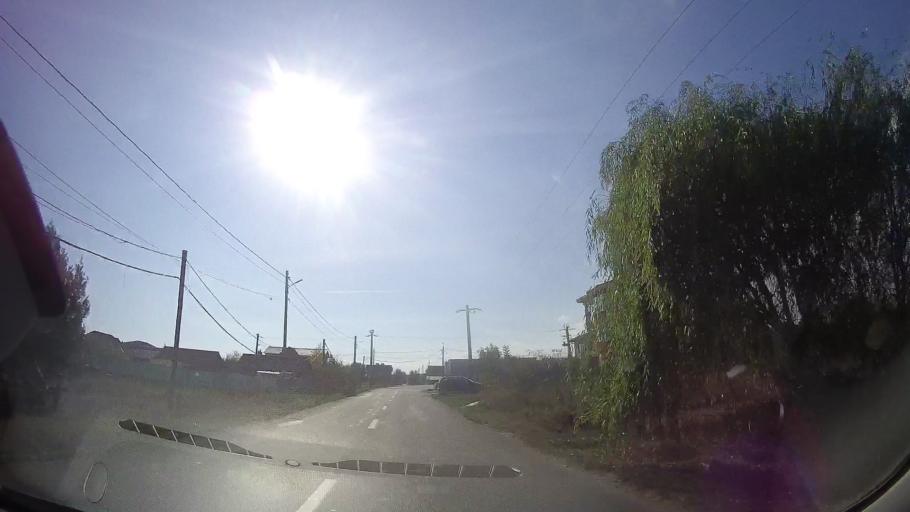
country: RO
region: Constanta
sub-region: Comuna Costinesti
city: Costinesti
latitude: 43.9553
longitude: 28.6324
